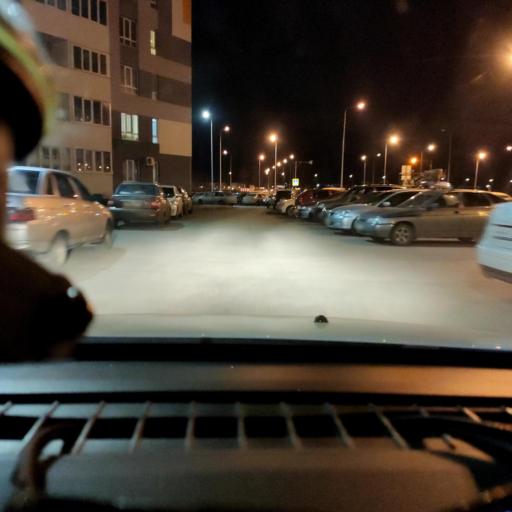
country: RU
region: Samara
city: Samara
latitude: 53.0944
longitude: 50.1606
